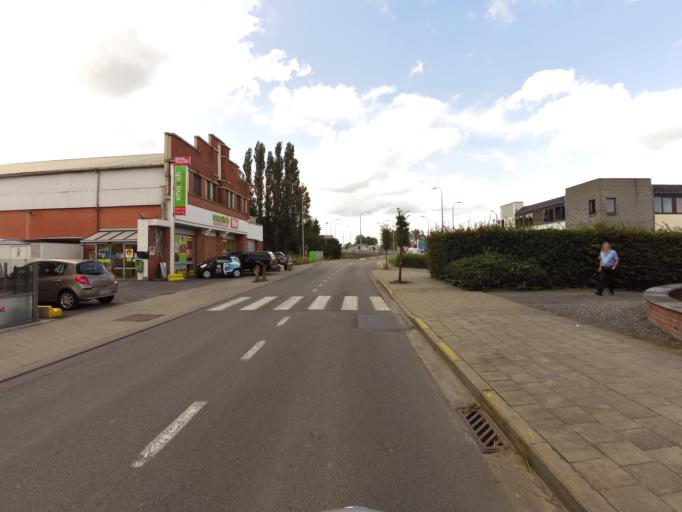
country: BE
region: Flanders
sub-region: Provincie West-Vlaanderen
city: Anzegem
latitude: 50.7913
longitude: 3.5074
